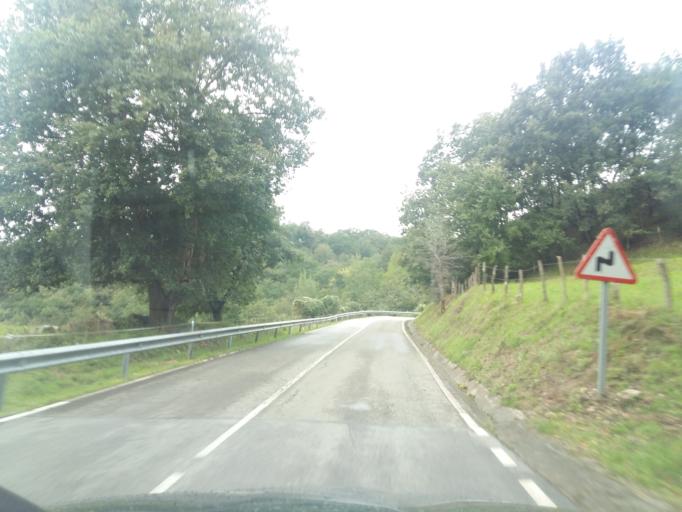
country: ES
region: Cantabria
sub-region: Provincia de Cantabria
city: Ramales de la Victoria
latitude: 43.1918
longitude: -3.5376
